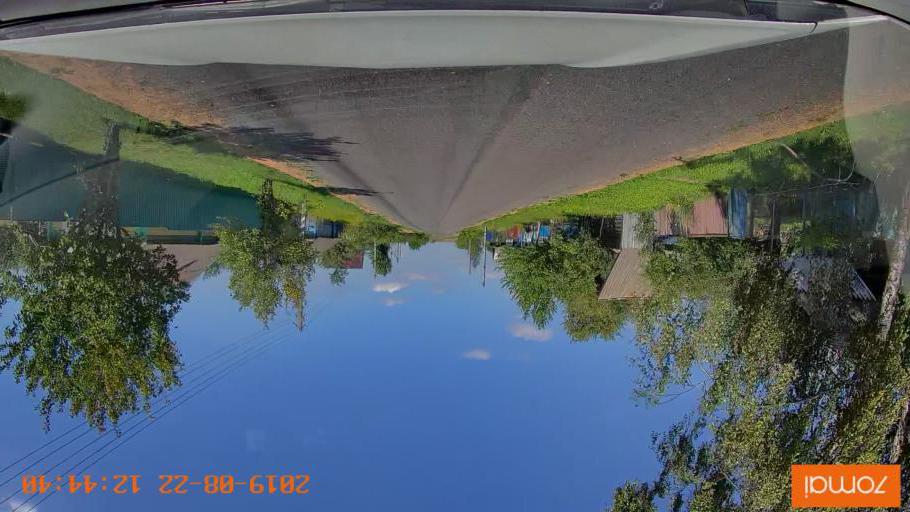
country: BY
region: Minsk
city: Prawdzinski
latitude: 53.4521
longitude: 27.6123
